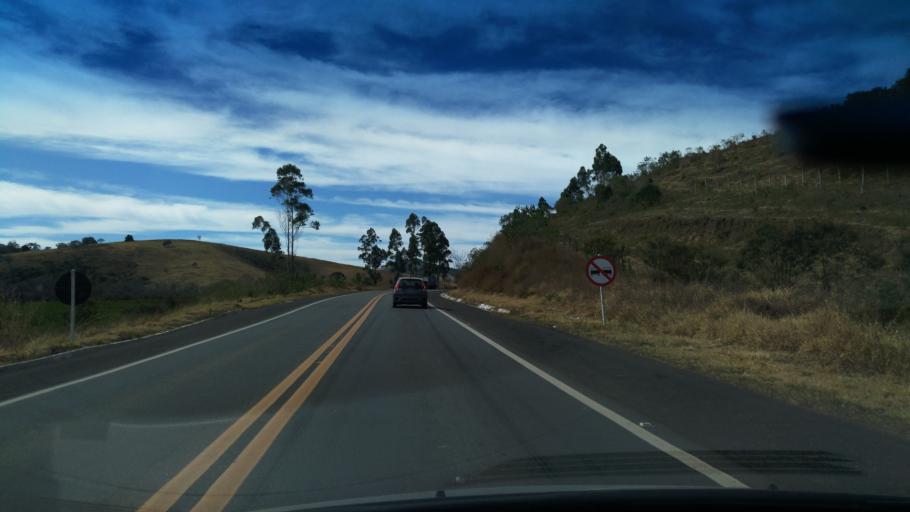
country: BR
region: Minas Gerais
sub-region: Borda Da Mata
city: Borda da Mata
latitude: -22.0742
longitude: -46.2610
